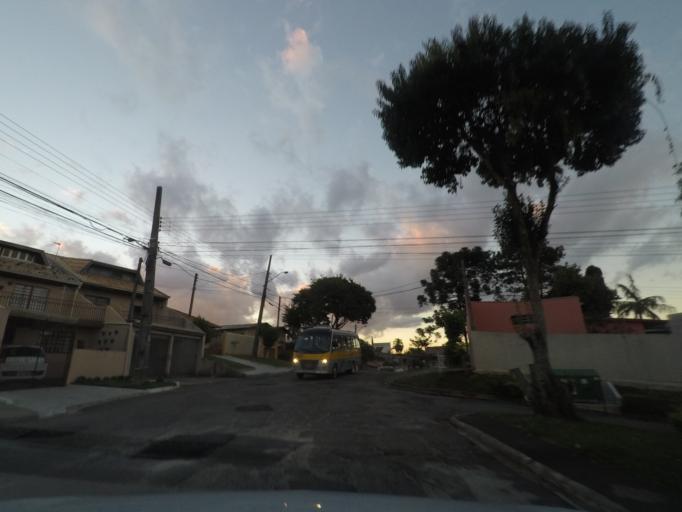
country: BR
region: Parana
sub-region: Sao Jose Dos Pinhais
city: Sao Jose dos Pinhais
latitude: -25.5039
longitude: -49.2636
